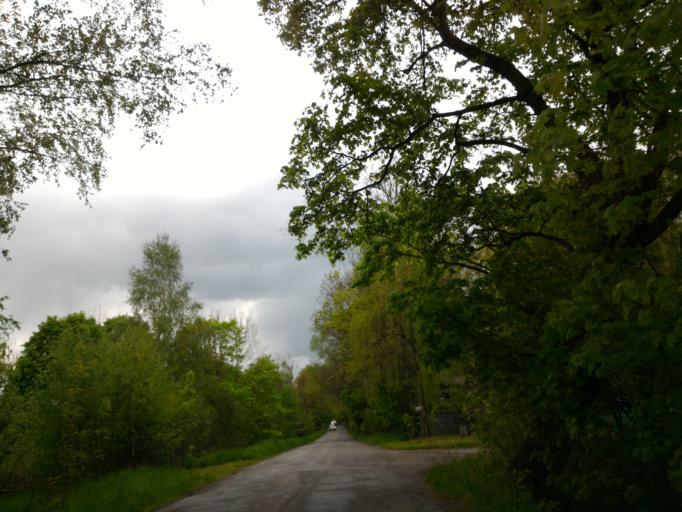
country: CZ
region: Vysocina
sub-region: Okres Havlickuv Brod
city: Svetla nad Sazavou
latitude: 49.6164
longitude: 15.4046
